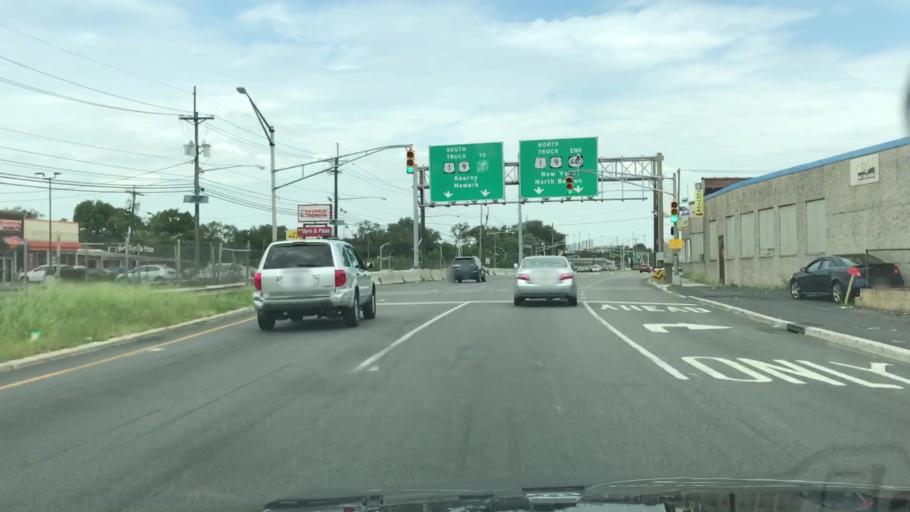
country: US
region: New Jersey
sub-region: Hudson County
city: Jersey City
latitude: 40.7220
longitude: -74.0919
